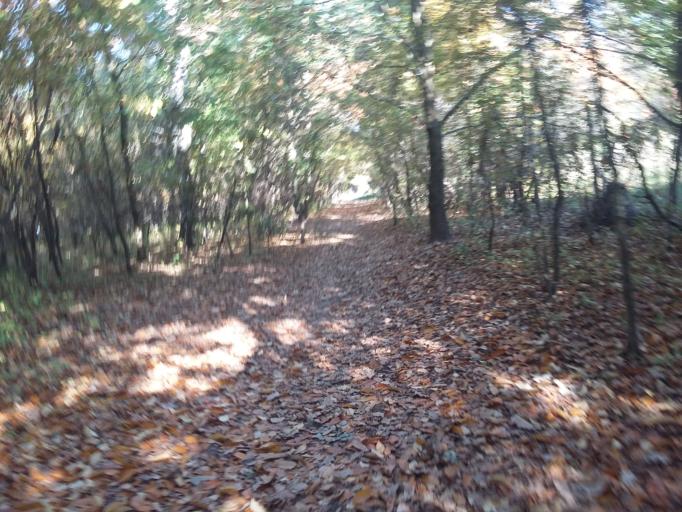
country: PL
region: Lodz Voivodeship
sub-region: Powiat pabianicki
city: Ksawerow
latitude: 51.7368
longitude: 19.4050
